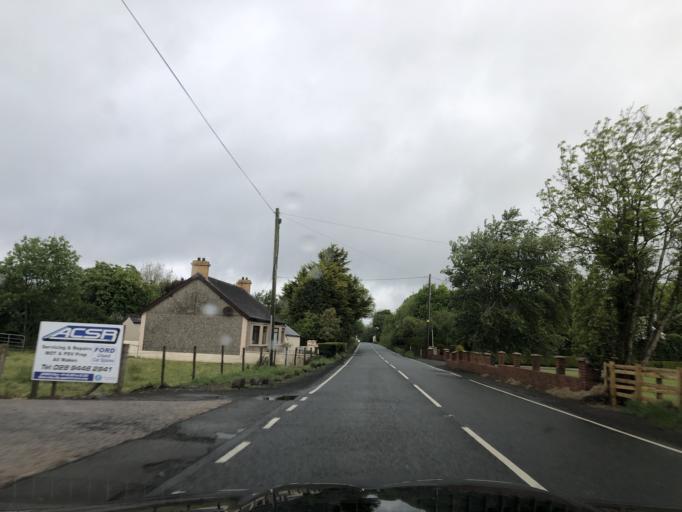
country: GB
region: Northern Ireland
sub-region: Antrim Borough
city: Antrim
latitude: 54.6749
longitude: -6.2213
